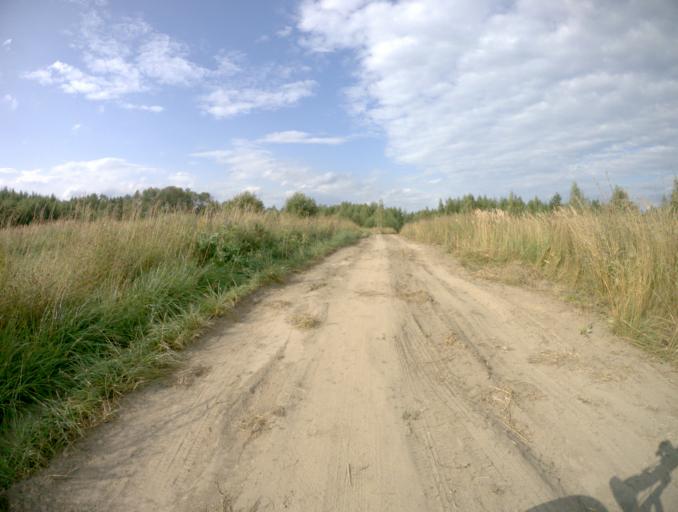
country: RU
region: Vladimir
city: Raduzhnyy
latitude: 55.9851
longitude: 40.3773
